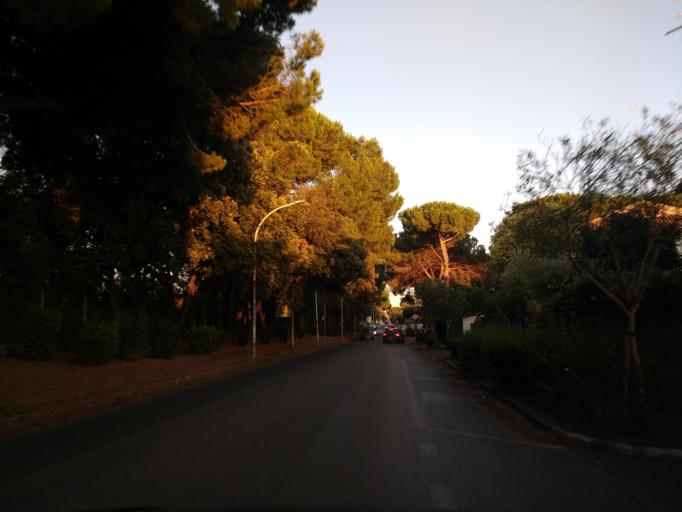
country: IT
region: Latium
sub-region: Citta metropolitana di Roma Capitale
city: Acilia-Castel Fusano-Ostia Antica
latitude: 41.7602
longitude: 12.3626
